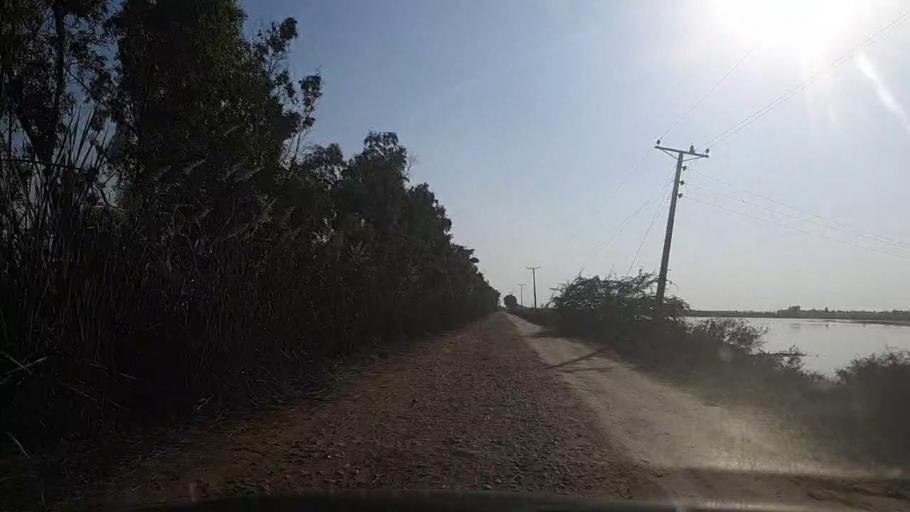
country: PK
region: Sindh
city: Gharo
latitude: 24.7217
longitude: 67.6911
